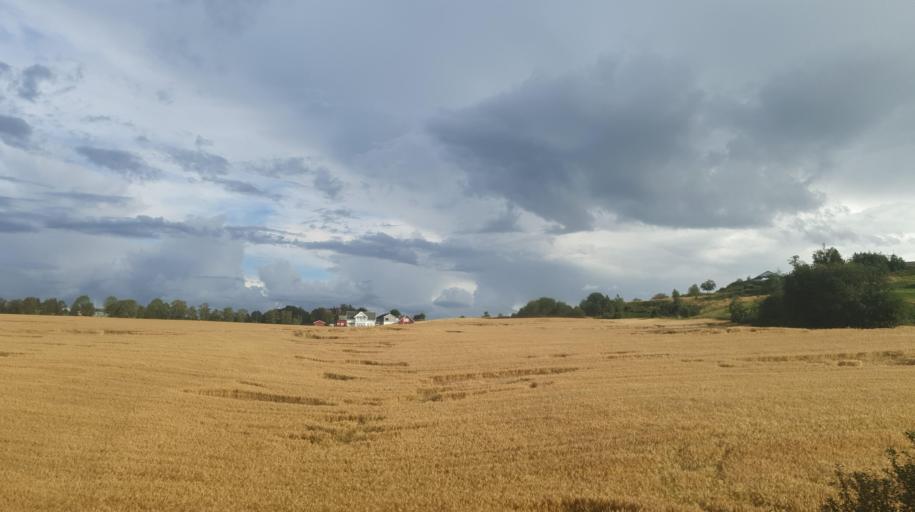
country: NO
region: Nord-Trondelag
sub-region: Levanger
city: Skogn
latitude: 63.7150
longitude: 11.2081
